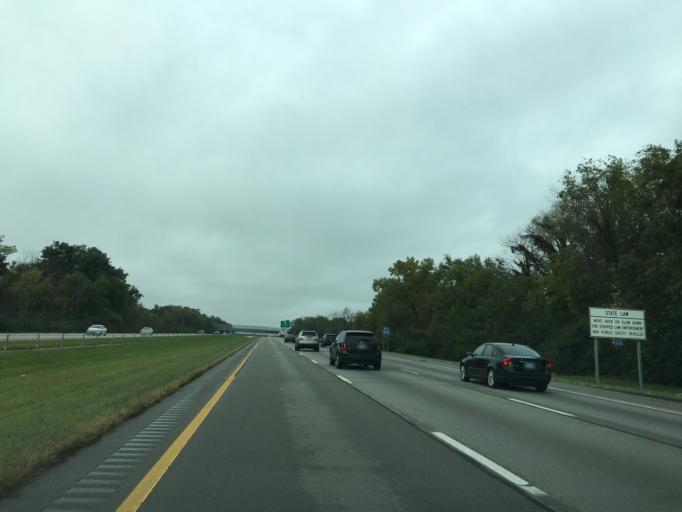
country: US
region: Ohio
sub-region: Hamilton County
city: Pleasant Run Farm
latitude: 39.2967
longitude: -84.5350
